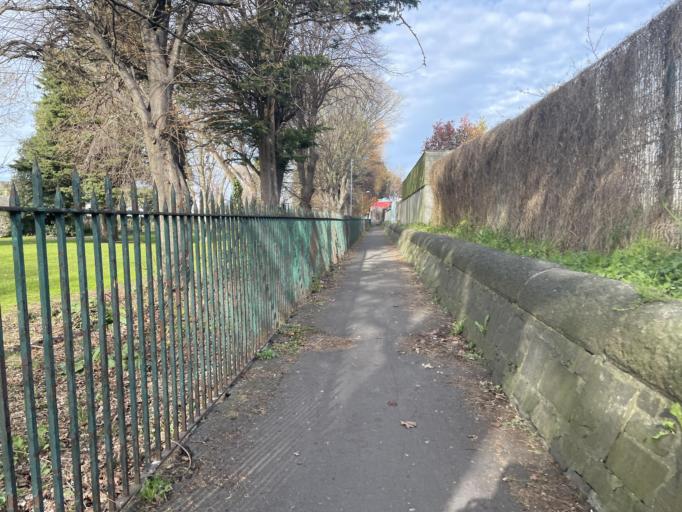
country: IE
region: Leinster
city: Ringsend
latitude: 53.3419
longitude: -6.2181
